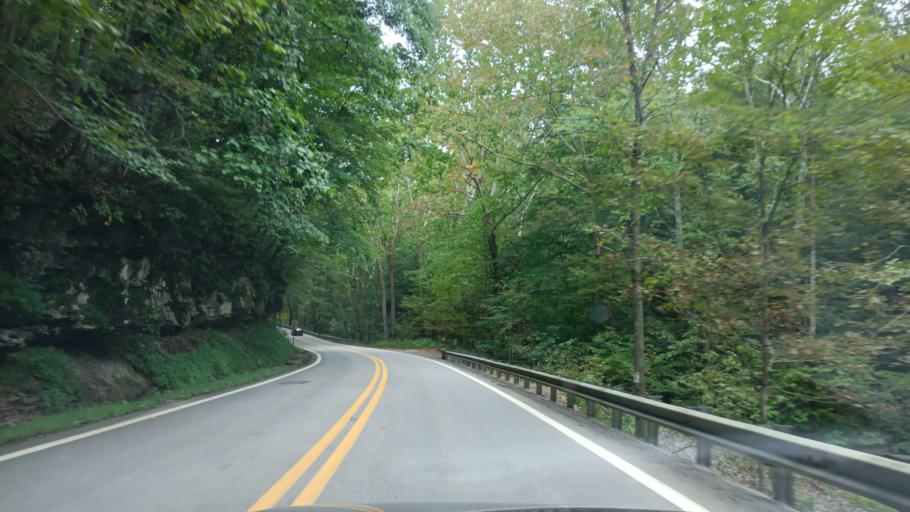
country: US
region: West Virginia
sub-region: Taylor County
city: Grafton
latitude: 39.3413
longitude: -79.9341
